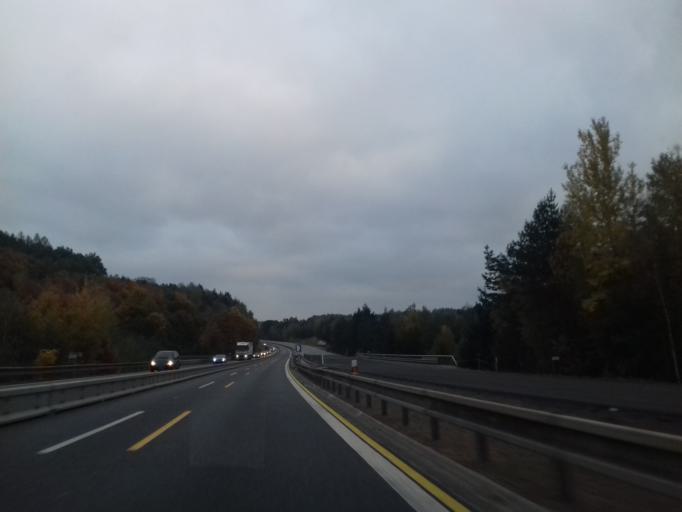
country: CZ
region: Central Bohemia
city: Trhovy Stepanov
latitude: 49.7494
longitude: 15.0275
